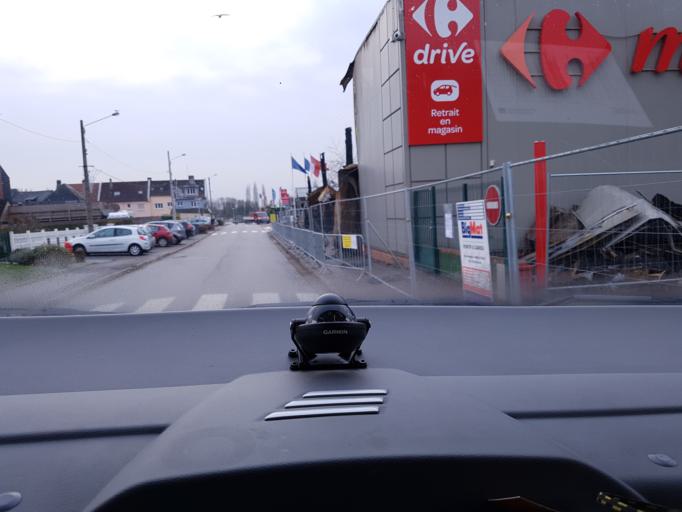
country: FR
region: Haute-Normandie
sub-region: Departement de la Seine-Maritime
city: Duclair
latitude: 49.4814
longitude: 0.8723
